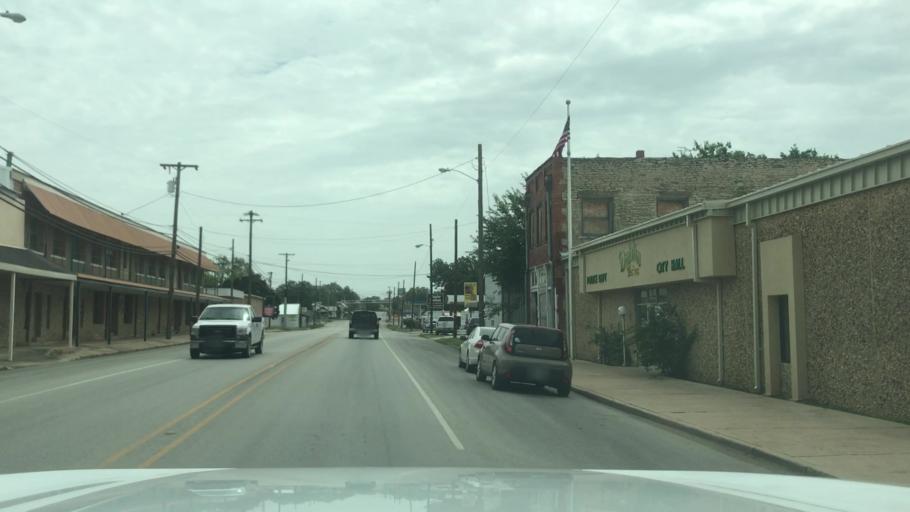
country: US
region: Texas
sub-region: Erath County
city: Dublin
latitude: 32.0849
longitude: -98.3413
